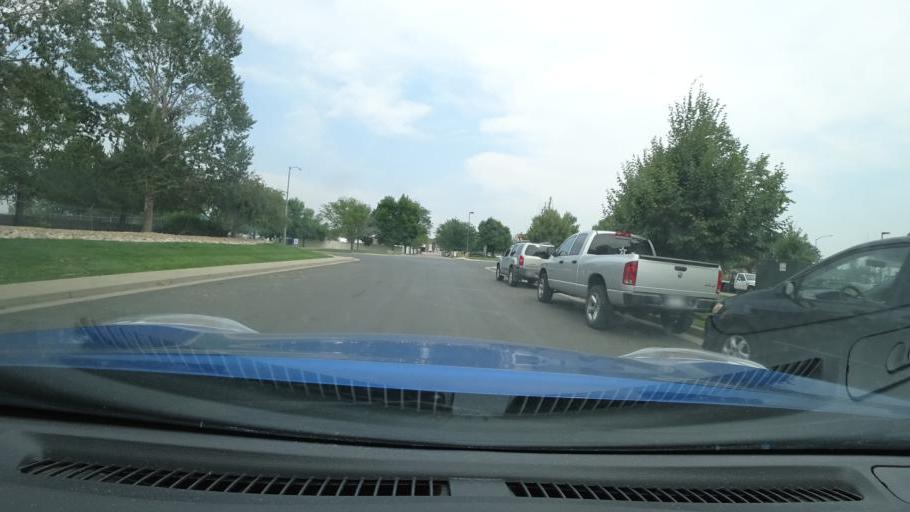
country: US
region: Colorado
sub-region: Adams County
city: Aurora
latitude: 39.7516
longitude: -104.7804
